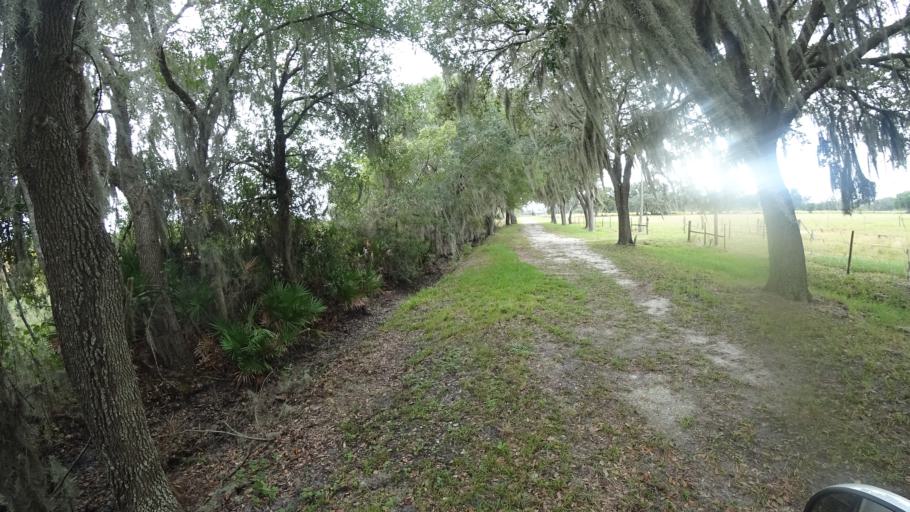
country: US
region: Florida
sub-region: Hillsborough County
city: Wimauma
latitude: 27.6016
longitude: -82.1862
